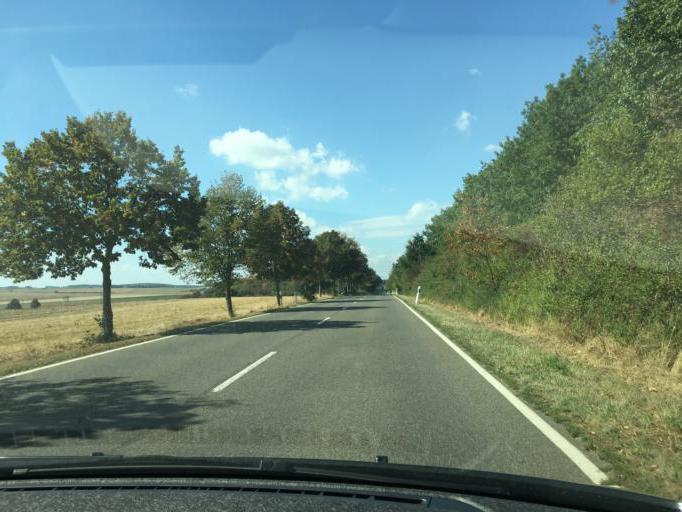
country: DE
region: North Rhine-Westphalia
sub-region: Regierungsbezirk Koln
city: Vettweiss
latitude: 50.6705
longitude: 6.5933
